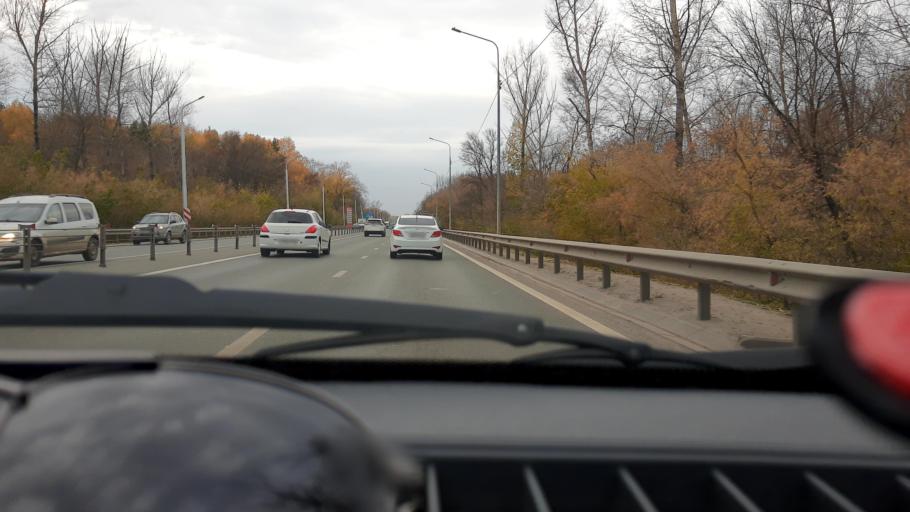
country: RU
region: Bashkortostan
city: Ufa
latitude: 54.7011
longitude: 55.9332
